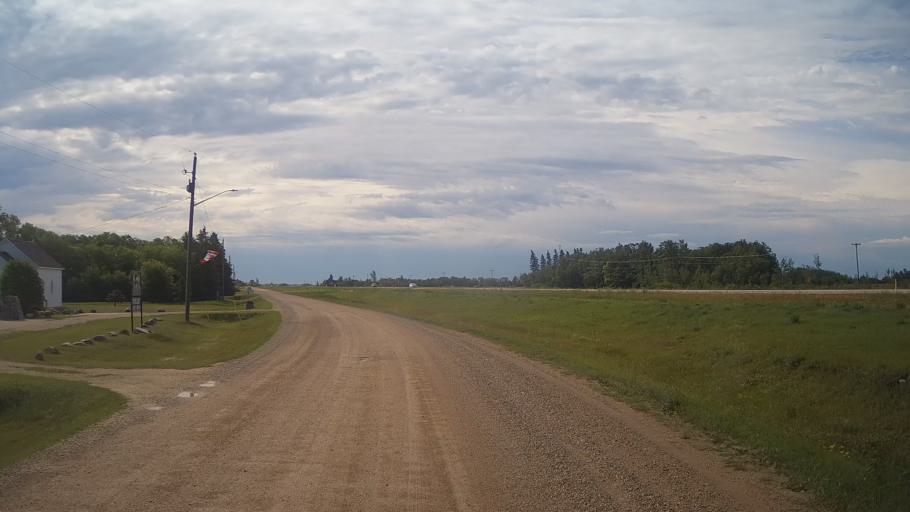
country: CA
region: Manitoba
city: Stonewall
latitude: 50.2038
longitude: -97.6559
